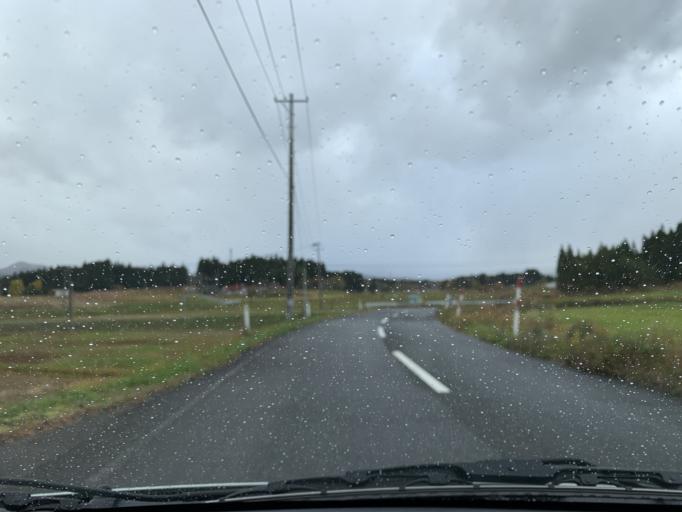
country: JP
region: Iwate
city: Mizusawa
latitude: 39.0889
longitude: 141.0009
